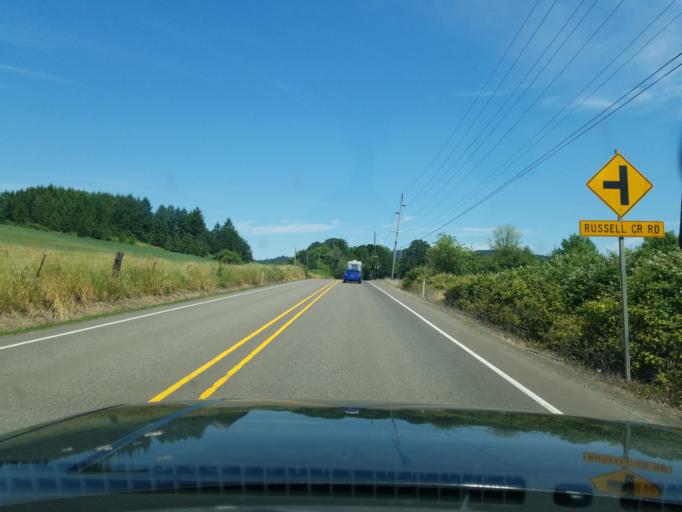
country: US
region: Oregon
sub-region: Yamhill County
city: Yamhill
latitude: 45.3599
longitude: -123.1689
